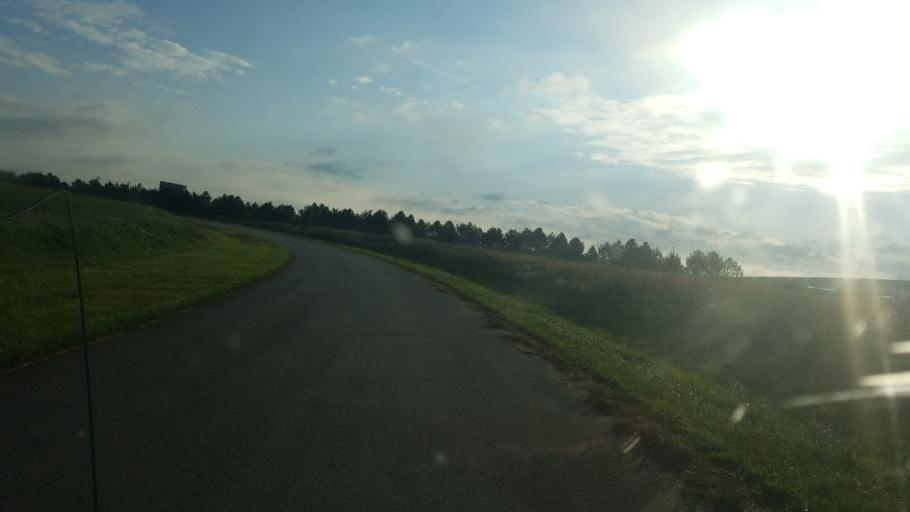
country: US
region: Ohio
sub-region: Wyandot County
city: Upper Sandusky
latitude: 40.8477
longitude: -83.3279
